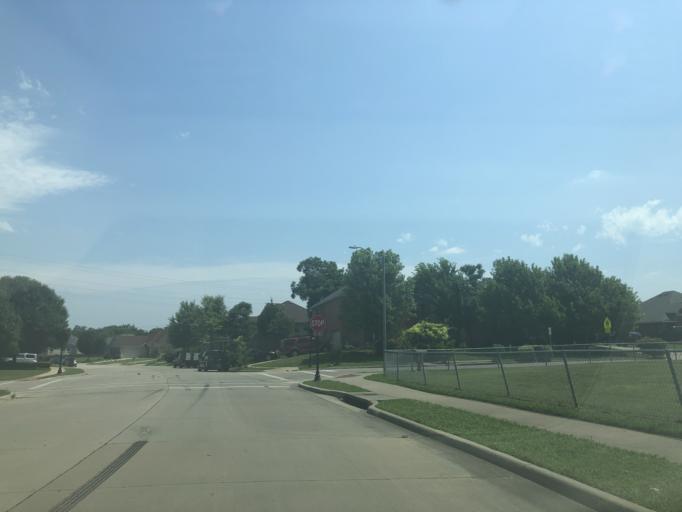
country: US
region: Texas
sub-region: Dallas County
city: Grand Prairie
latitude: 32.7266
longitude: -97.0001
